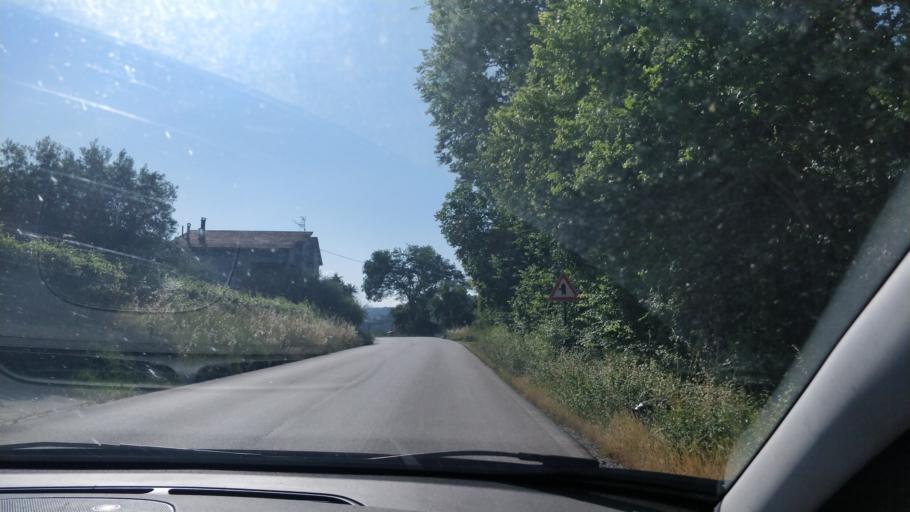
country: IT
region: The Marches
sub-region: Provincia di Ascoli Piceno
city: Cupra Marittima
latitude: 43.0353
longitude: 13.8438
